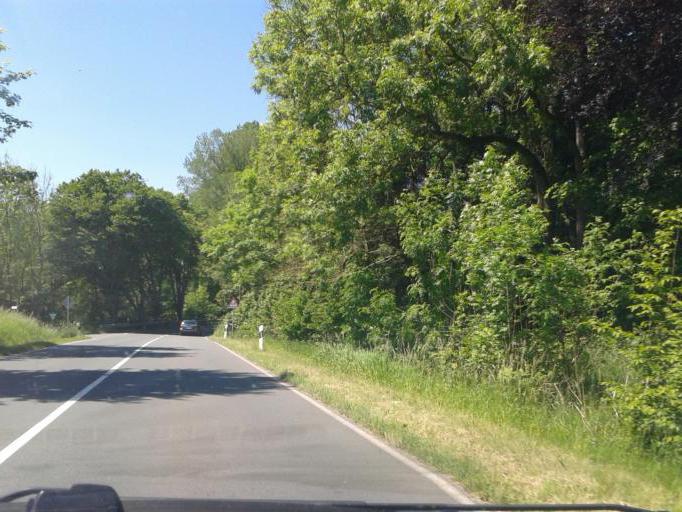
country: DE
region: North Rhine-Westphalia
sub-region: Regierungsbezirk Detmold
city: Blomberg
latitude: 51.9241
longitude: 9.1078
